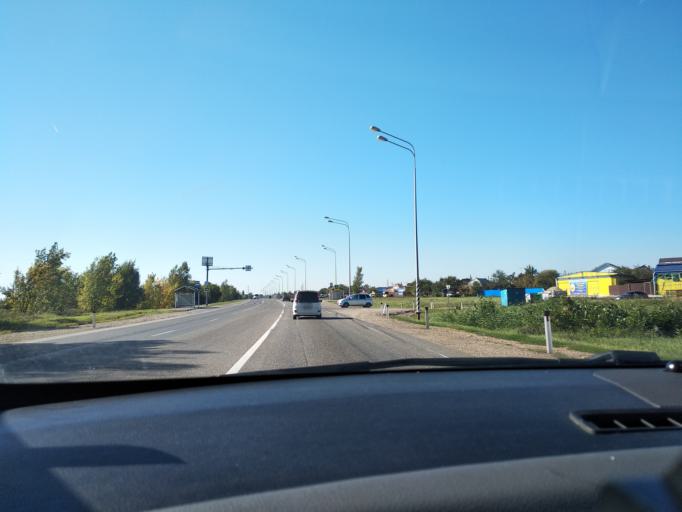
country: RU
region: Krasnodarskiy
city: Agronom
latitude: 45.1681
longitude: 39.0904
